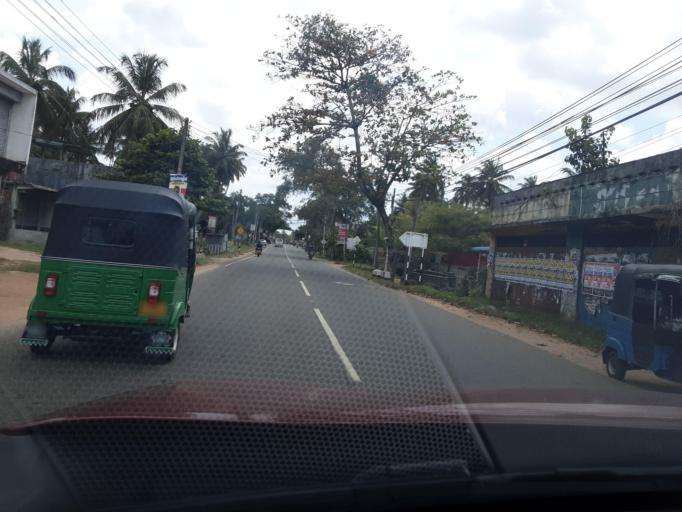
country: LK
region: North Western
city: Kuliyapitiya
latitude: 7.4514
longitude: 80.1688
